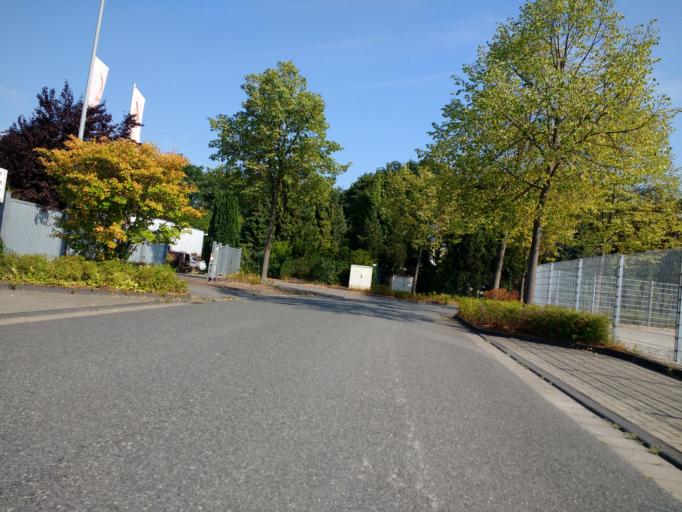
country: DE
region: Lower Saxony
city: Gifhorn
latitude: 52.4581
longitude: 10.5377
